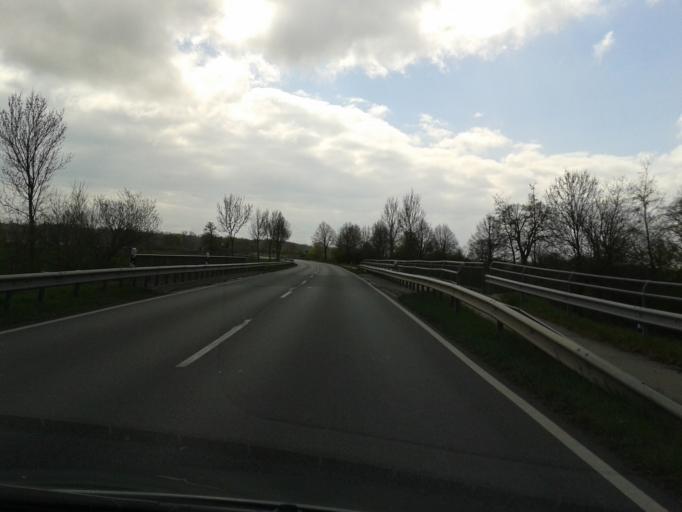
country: DE
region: Lower Saxony
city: Lubbow
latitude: 52.9038
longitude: 11.1792
